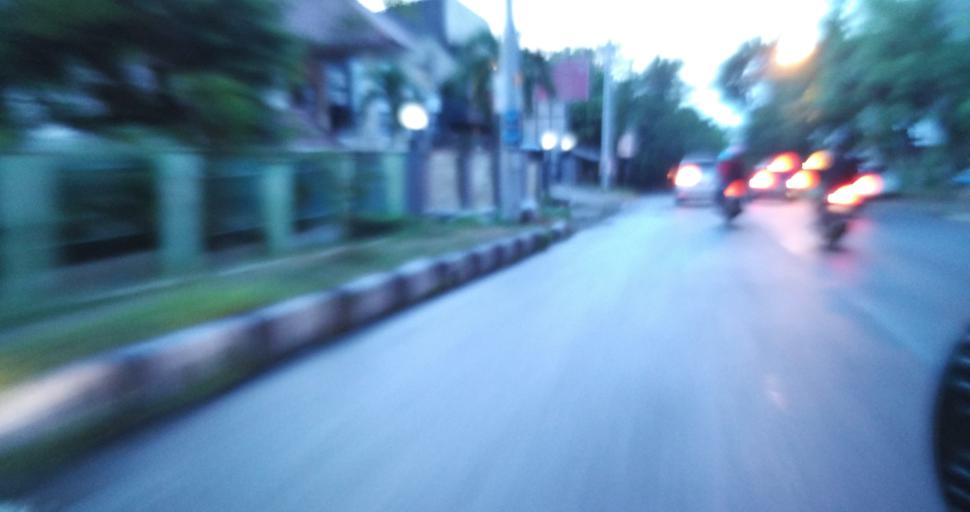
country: ID
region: Central Java
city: Semarang
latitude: -7.0372
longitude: 110.4176
